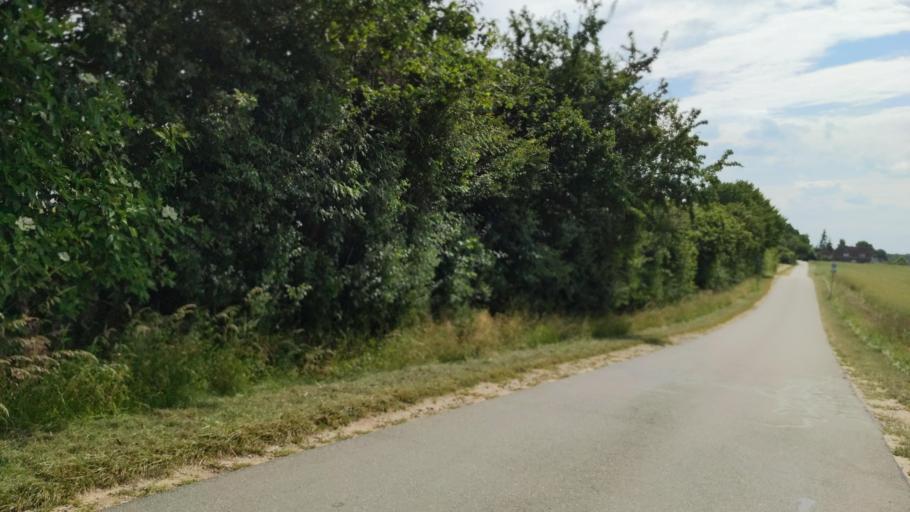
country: DE
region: Mecklenburg-Vorpommern
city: Dassow
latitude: 53.9723
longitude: 10.9714
